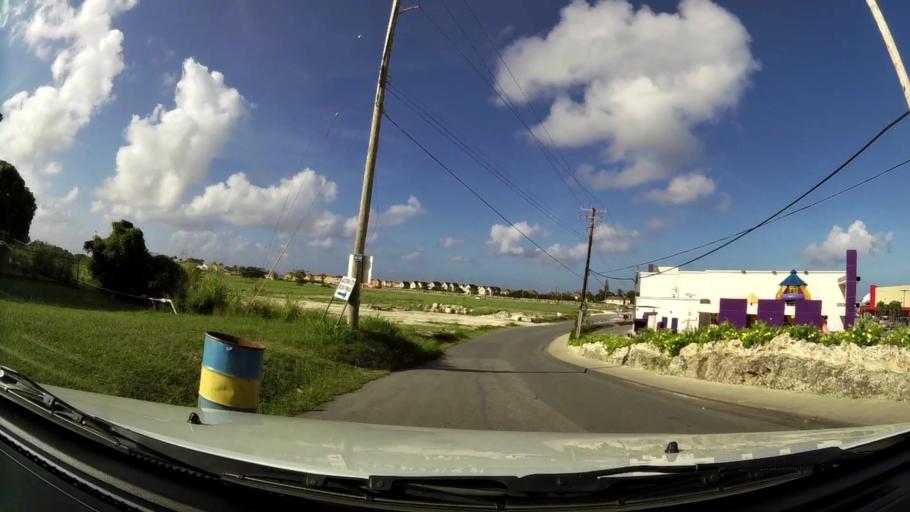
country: BB
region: Saint James
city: Holetown
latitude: 13.1540
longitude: -59.6110
